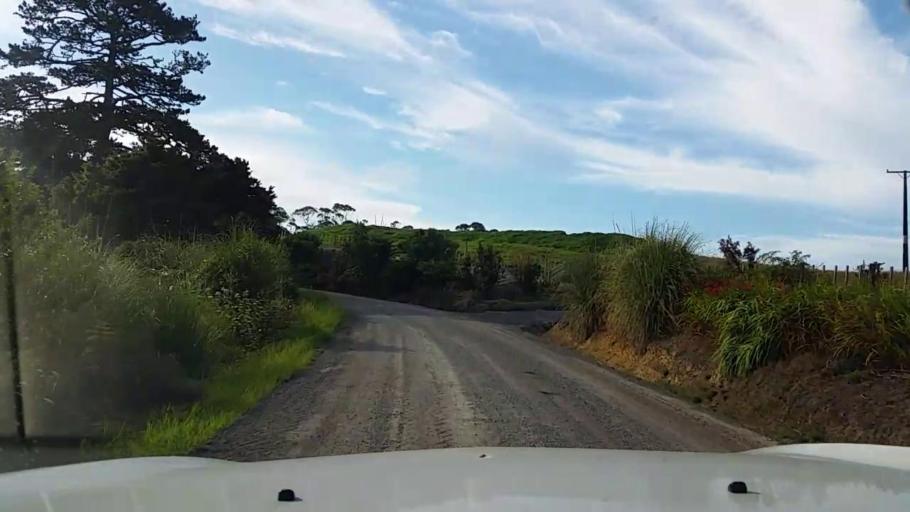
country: NZ
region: Northland
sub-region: Whangarei
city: Maungatapere
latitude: -35.6685
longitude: 174.1746
